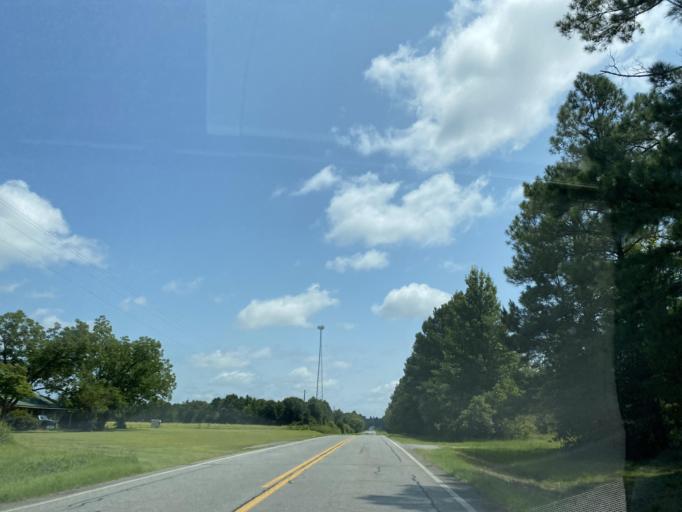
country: US
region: Georgia
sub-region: Wilcox County
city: Abbeville
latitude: 31.9990
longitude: -83.1790
